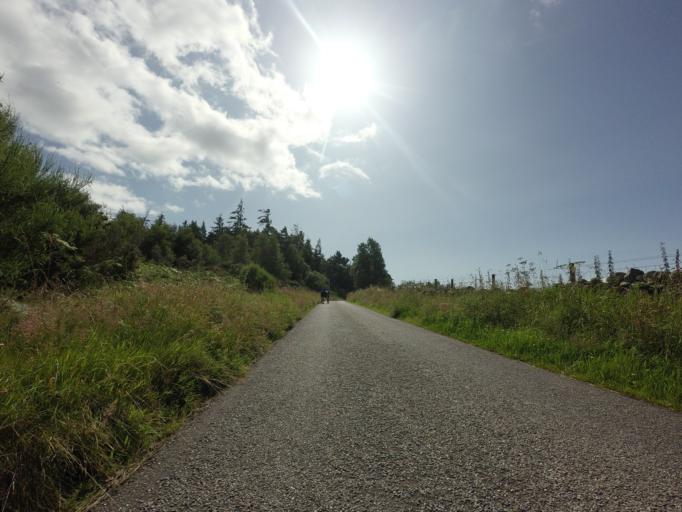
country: GB
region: Scotland
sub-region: Highland
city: Nairn
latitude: 57.5312
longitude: -3.8631
